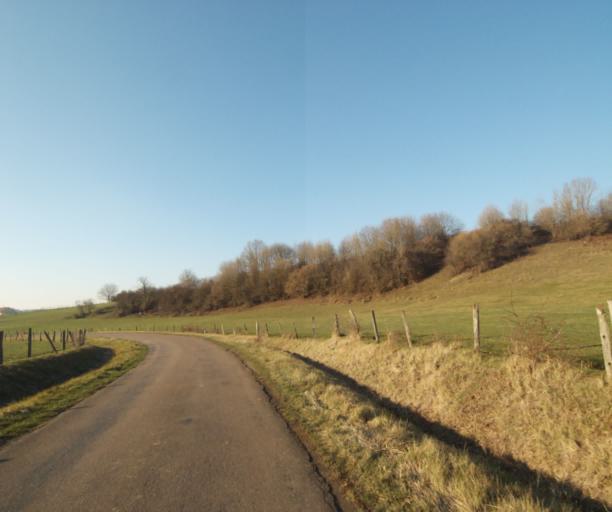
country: FR
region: Champagne-Ardenne
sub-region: Departement de la Haute-Marne
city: Chevillon
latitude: 48.5398
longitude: 5.1115
